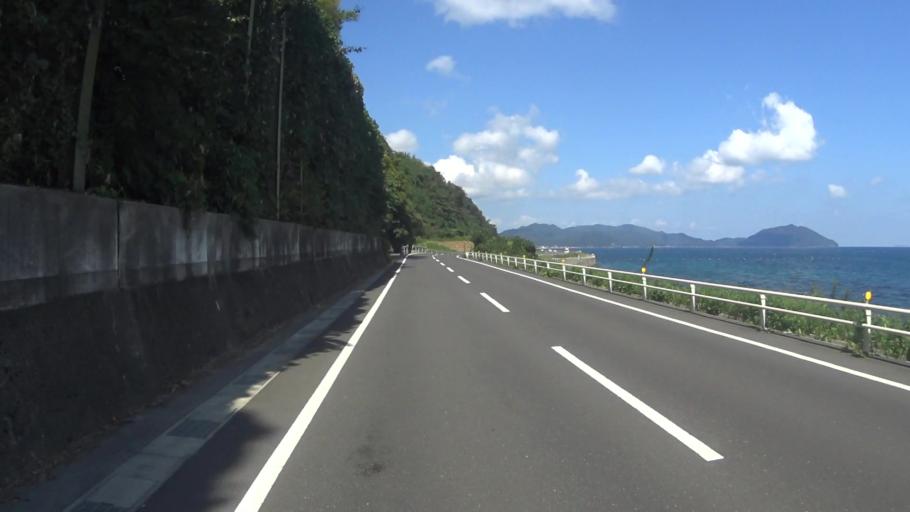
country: JP
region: Kyoto
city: Miyazu
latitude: 35.6300
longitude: 135.2456
